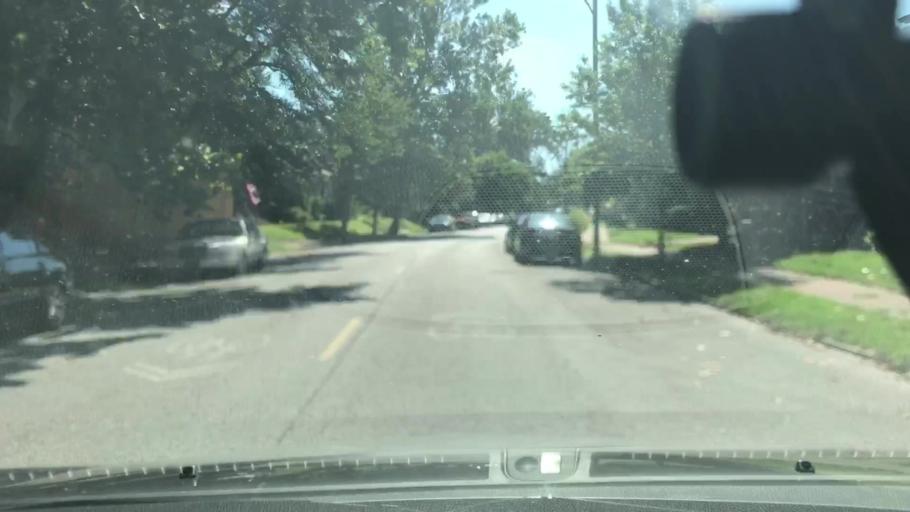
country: US
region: Missouri
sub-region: Saint Louis County
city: Richmond Heights
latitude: 38.6115
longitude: -90.2920
